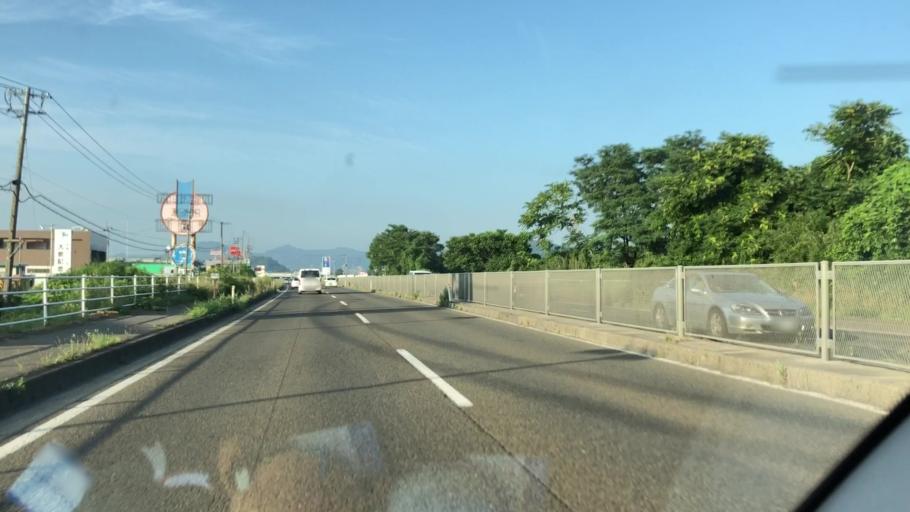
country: JP
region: Miyagi
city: Shiroishi
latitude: 38.0317
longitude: 140.6339
